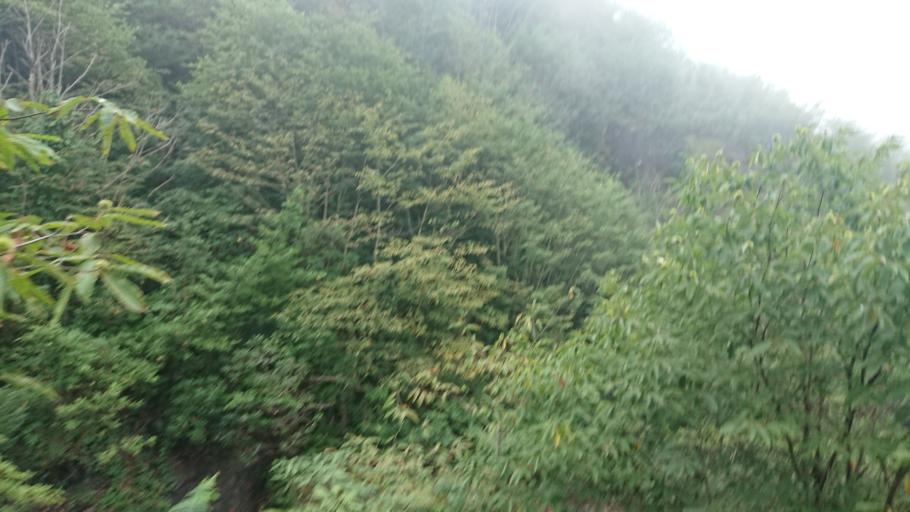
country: TR
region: Rize
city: Hemsin
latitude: 41.0454
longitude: 40.8095
